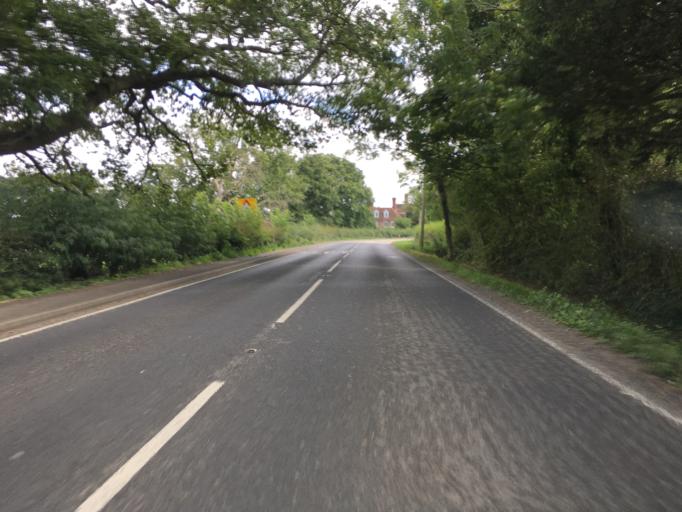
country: GB
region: England
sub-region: Kent
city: Tenterden
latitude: 51.1115
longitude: 0.6445
